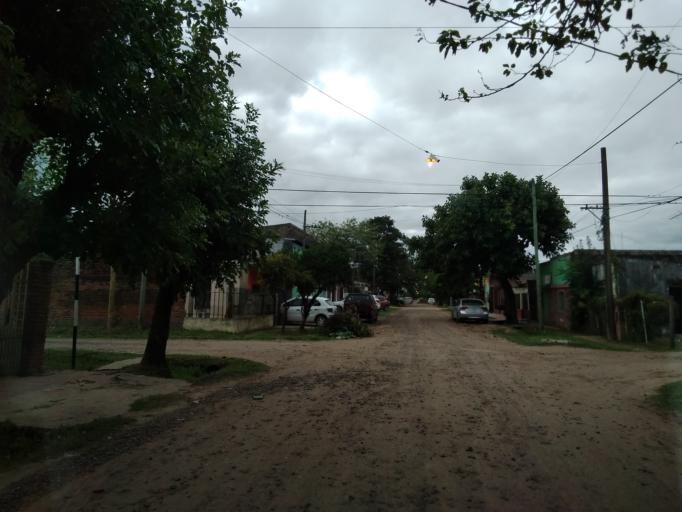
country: AR
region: Corrientes
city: Corrientes
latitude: -27.4780
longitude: -58.8122
